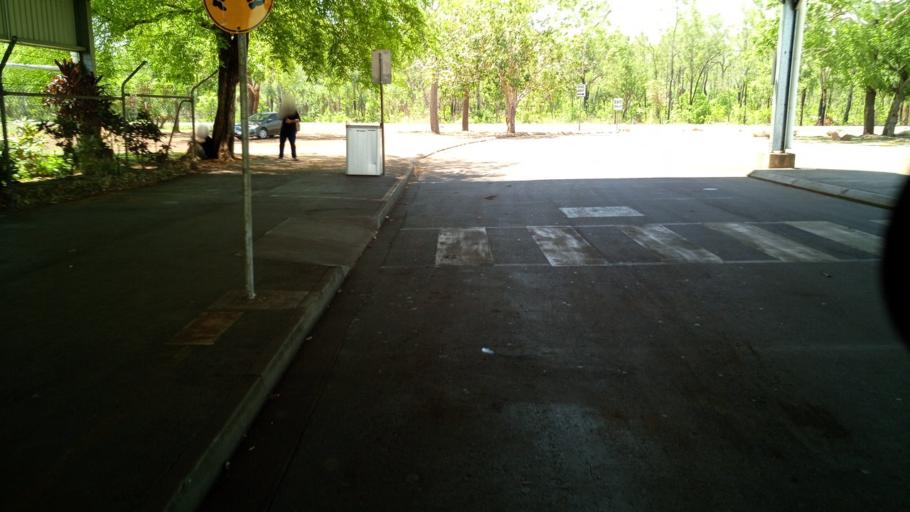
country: AU
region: Northern Territory
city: Alyangula
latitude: -13.9736
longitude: 136.4575
